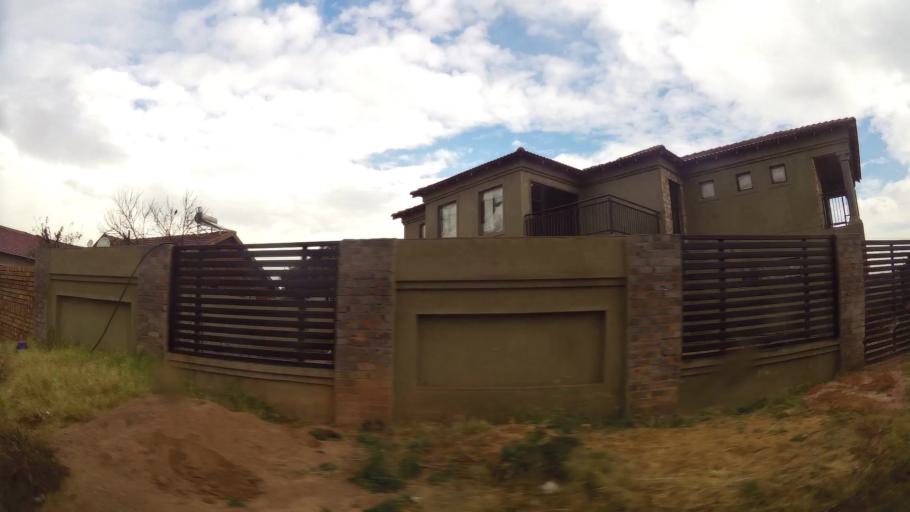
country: ZA
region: Gauteng
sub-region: Ekurhuleni Metropolitan Municipality
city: Germiston
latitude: -26.3259
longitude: 28.1979
